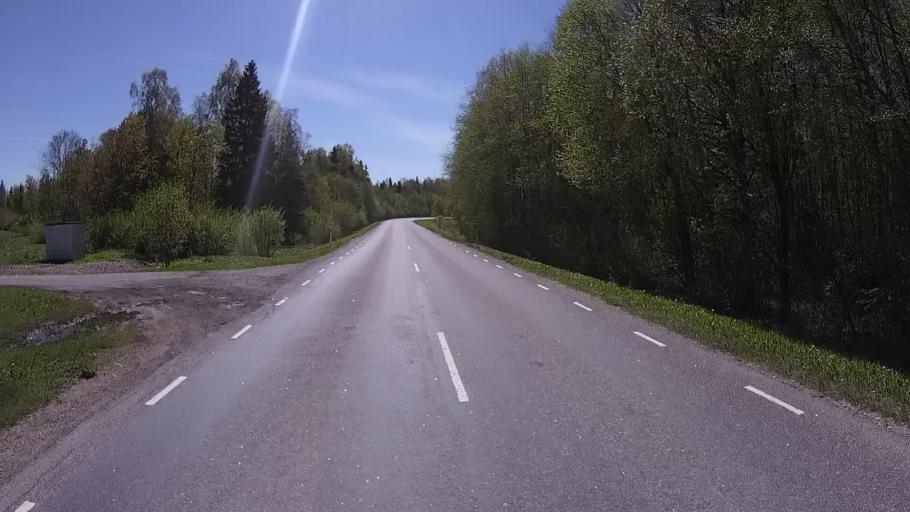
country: EE
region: Harju
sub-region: Raasiku vald
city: Raasiku
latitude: 59.0852
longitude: 25.1763
